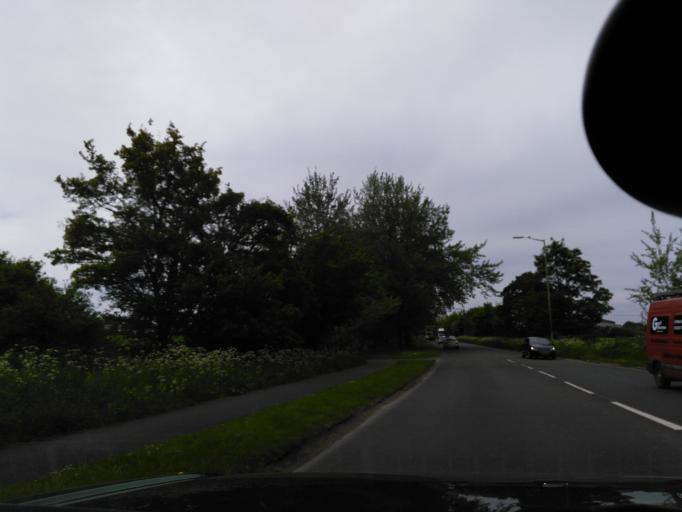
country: GB
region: England
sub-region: Wiltshire
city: Melksham
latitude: 51.3635
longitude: -2.1271
